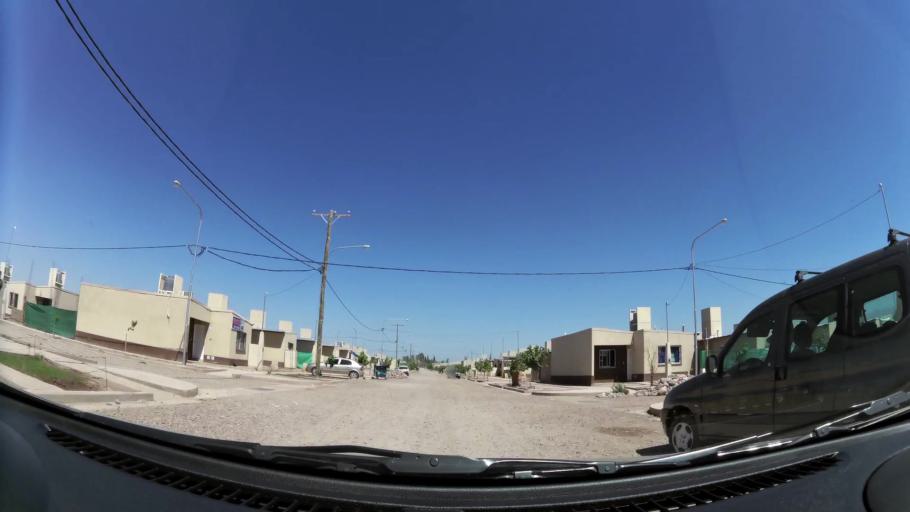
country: AR
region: Mendoza
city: Villa Nueva
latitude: -32.8756
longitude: -68.7891
